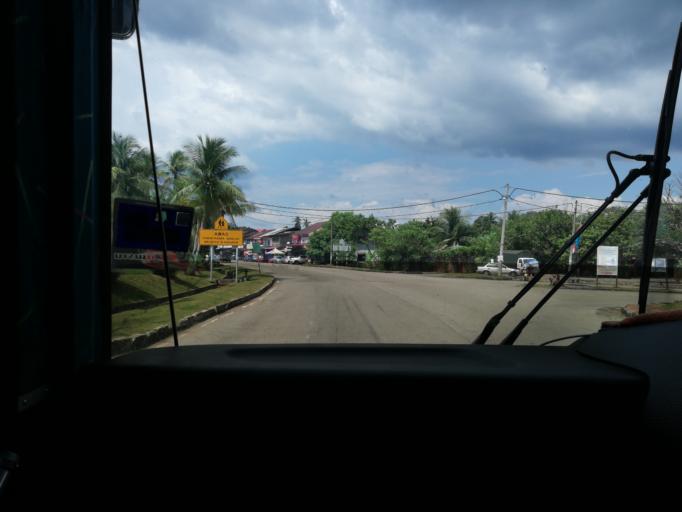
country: MY
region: Perak
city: Parit Buntar
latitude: 5.1388
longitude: 100.5896
